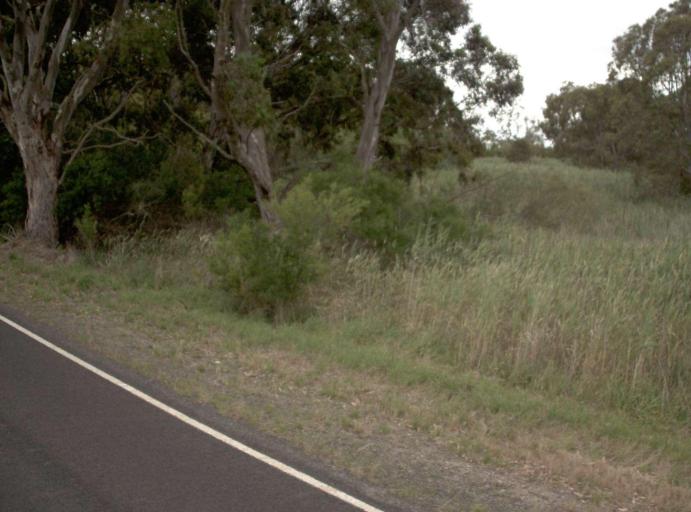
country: AU
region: Victoria
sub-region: Wellington
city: Sale
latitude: -38.0199
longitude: 147.1852
